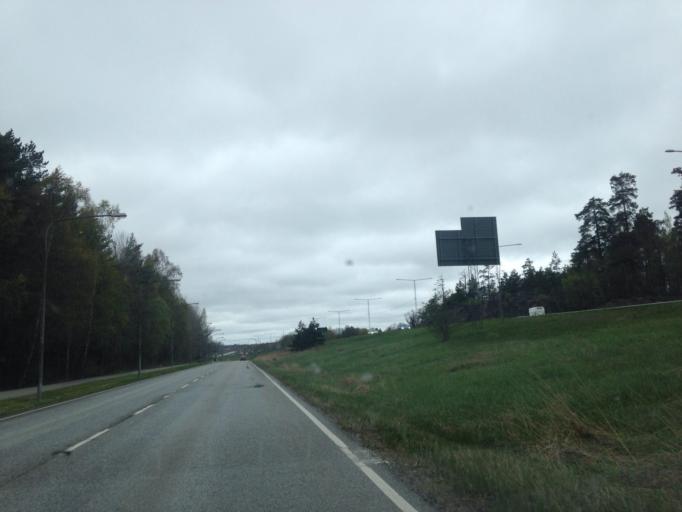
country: SE
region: Stockholm
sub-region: Nacka Kommun
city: Alta
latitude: 59.2588
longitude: 18.1633
